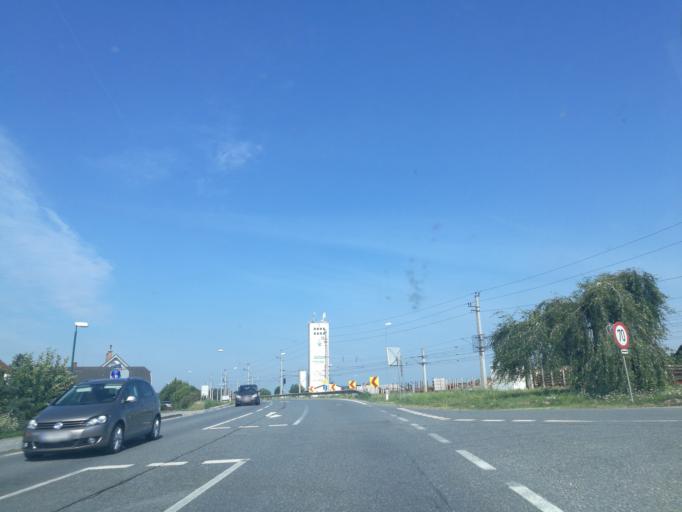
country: AT
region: Lower Austria
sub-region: Politischer Bezirk Zwettl
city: Gopfritz an der Wild
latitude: 48.7292
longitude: 15.3907
